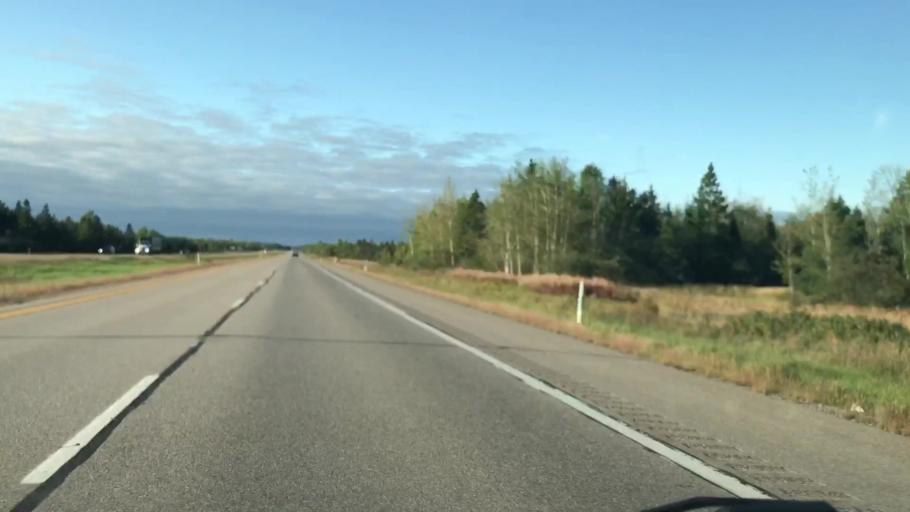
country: US
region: Michigan
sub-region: Chippewa County
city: Sault Ste. Marie
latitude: 46.4138
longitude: -84.3976
